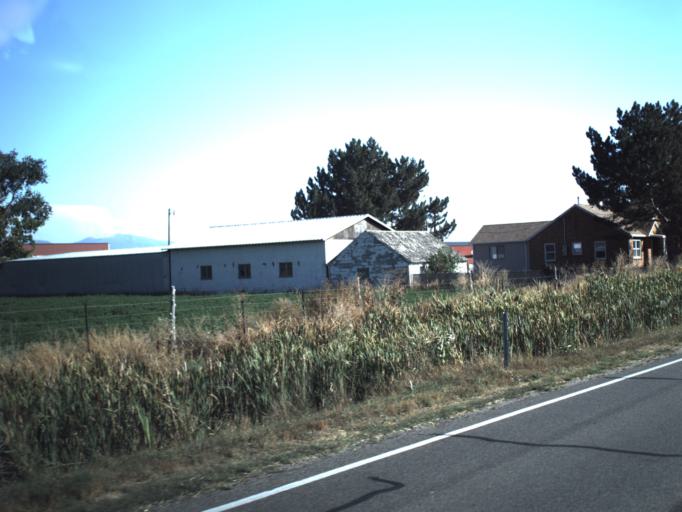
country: US
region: Utah
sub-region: Weber County
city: Hooper
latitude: 41.1531
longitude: -112.1229
